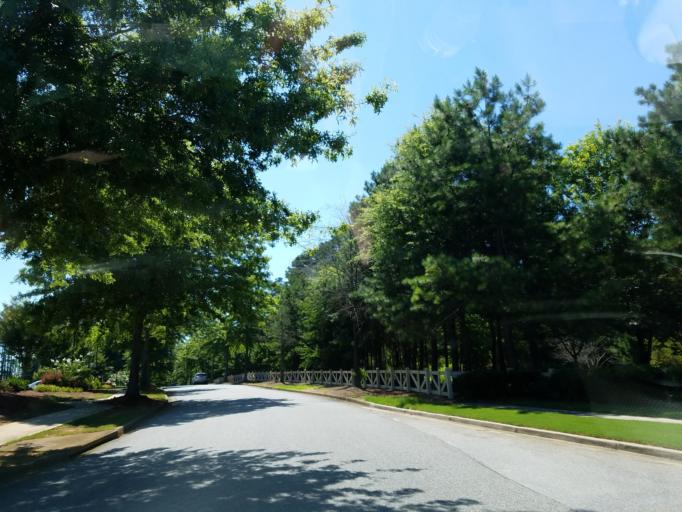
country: US
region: Georgia
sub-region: Forsyth County
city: Cumming
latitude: 34.3031
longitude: -84.0682
